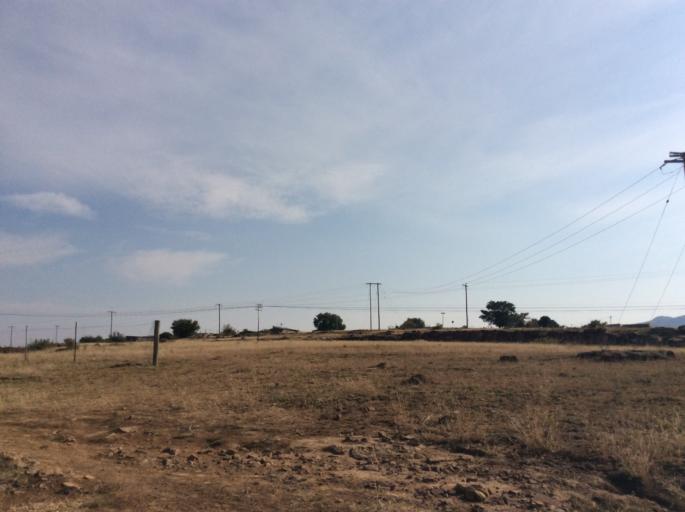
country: LS
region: Mafeteng
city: Mafeteng
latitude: -29.7216
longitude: 27.0136
